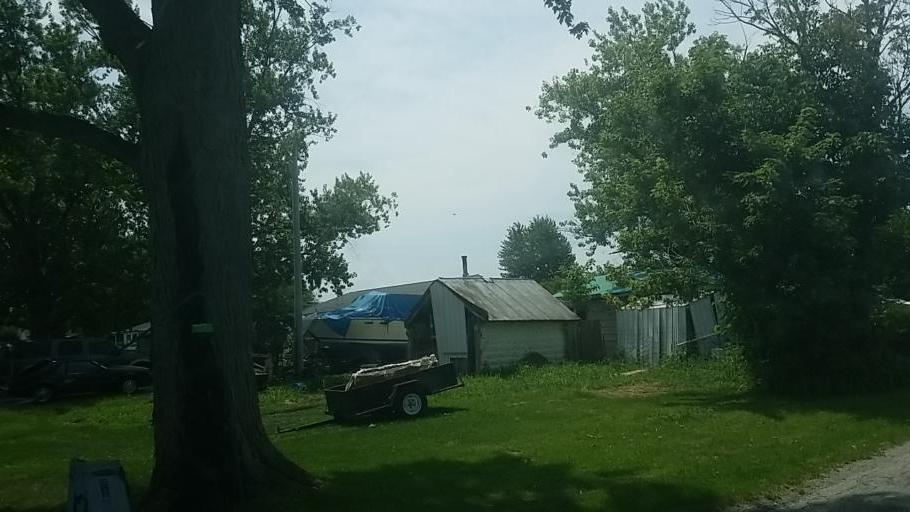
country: US
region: Ohio
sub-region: Union County
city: Richwood
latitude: 40.6074
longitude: -83.3240
